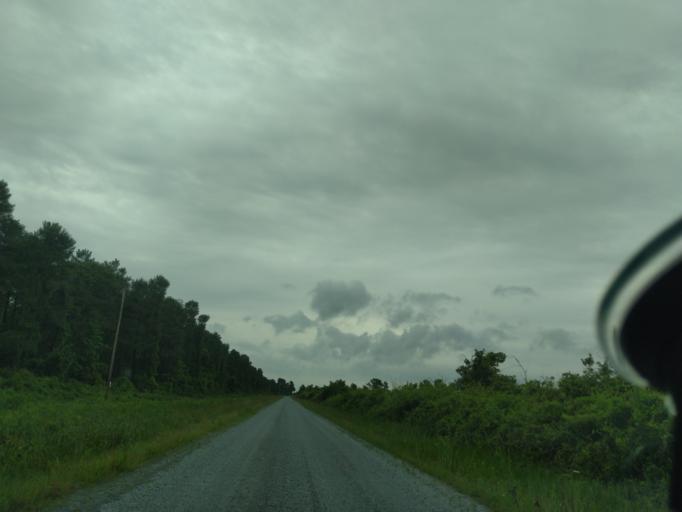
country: US
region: North Carolina
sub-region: Beaufort County
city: Belhaven
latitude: 35.7369
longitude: -76.4649
